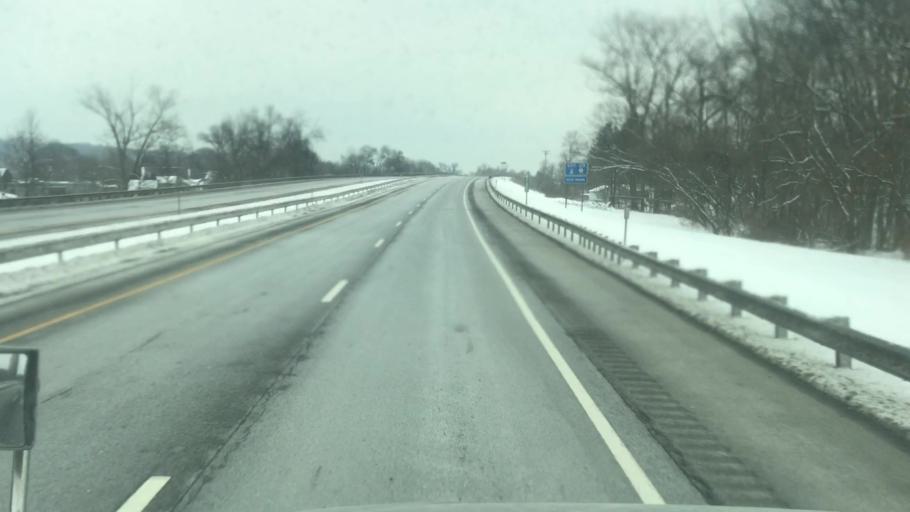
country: US
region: New York
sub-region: Montgomery County
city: Fonda
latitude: 42.9480
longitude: -74.3764
